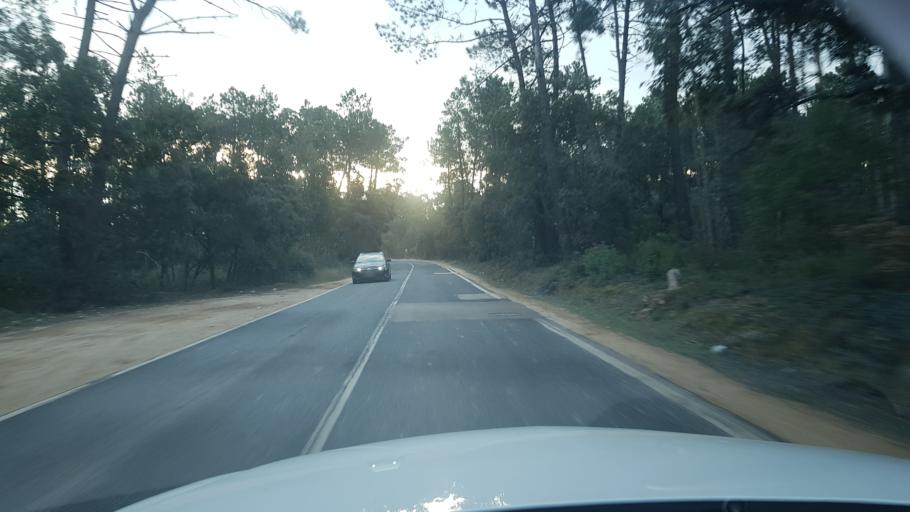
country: PT
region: Santarem
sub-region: Ourem
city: Fatima
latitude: 39.5834
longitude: -8.6246
